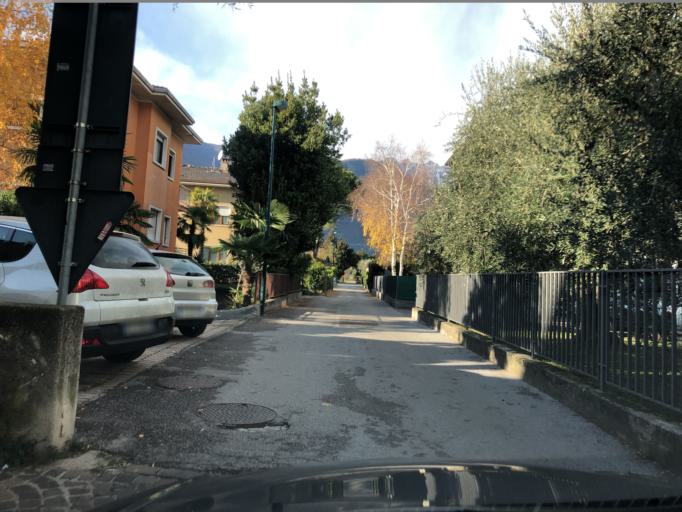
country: IT
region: Trentino-Alto Adige
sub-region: Provincia di Trento
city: Riva del Garda
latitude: 45.8898
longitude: 10.8621
